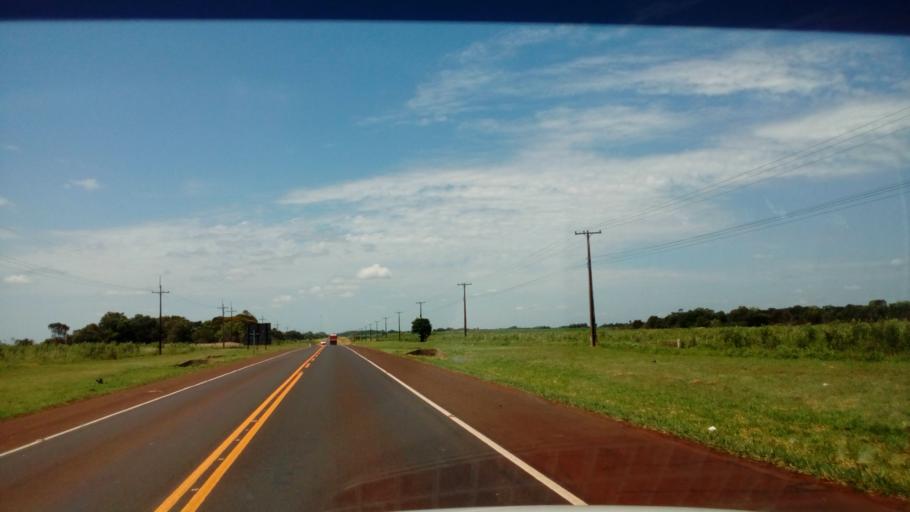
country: PY
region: Alto Parana
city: Colonia Yguazu
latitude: -25.5354
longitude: -54.9016
